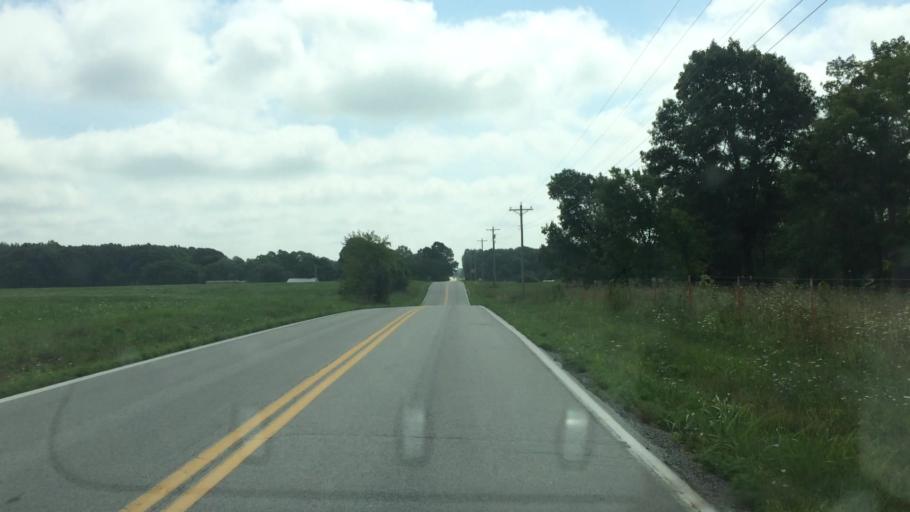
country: US
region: Missouri
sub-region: Greene County
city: Strafford
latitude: 37.2723
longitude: -93.2087
